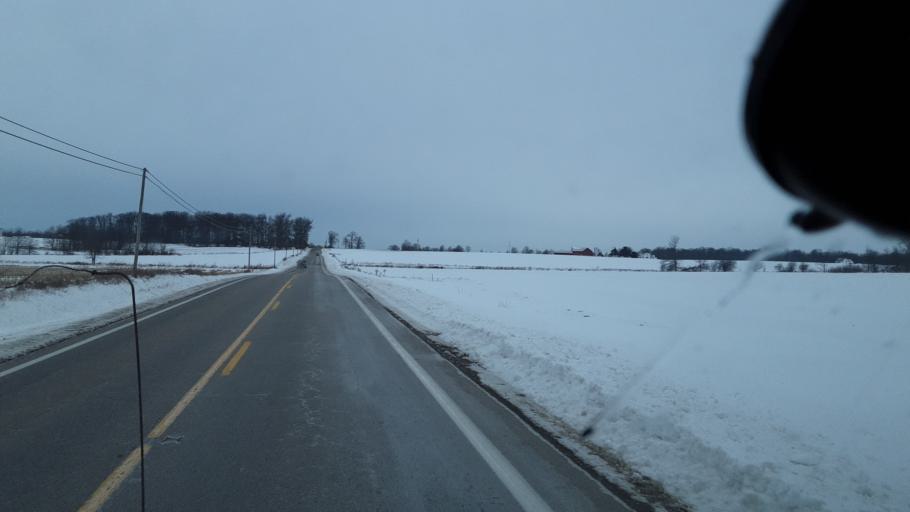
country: US
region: Ohio
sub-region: Union County
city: Marysville
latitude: 40.1793
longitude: -83.3345
